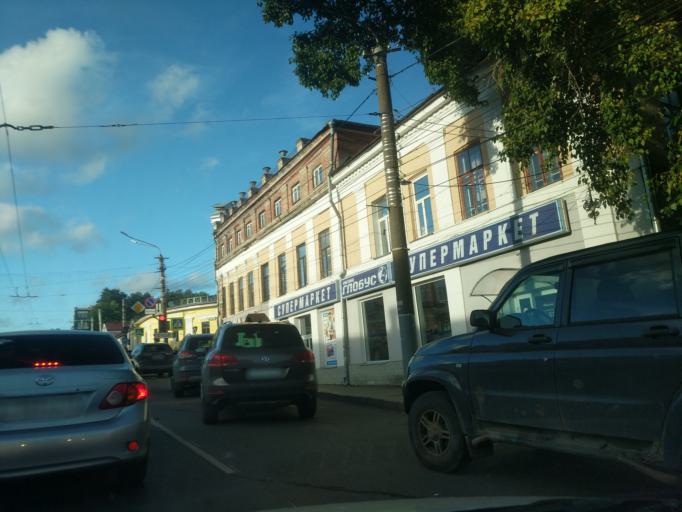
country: RU
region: Kirov
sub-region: Kirovo-Chepetskiy Rayon
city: Kirov
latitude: 58.6017
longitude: 49.6812
